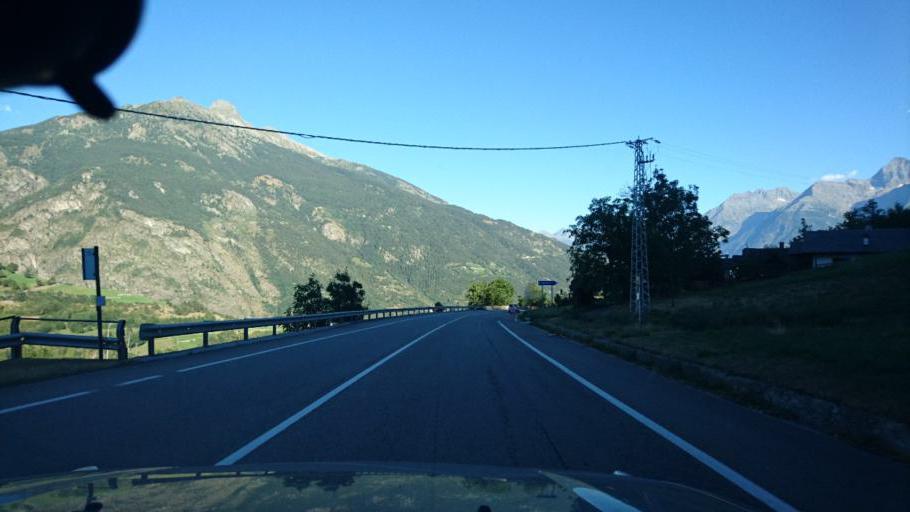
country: IT
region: Aosta Valley
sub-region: Valle d'Aosta
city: Allein
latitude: 45.7963
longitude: 7.2821
